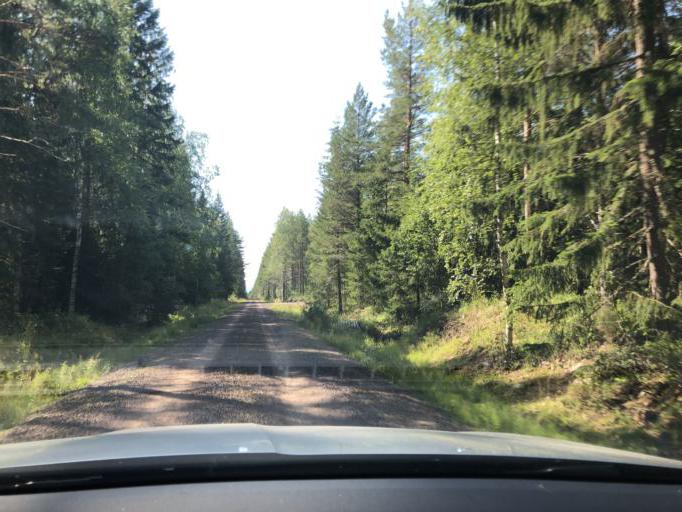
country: SE
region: Dalarna
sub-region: Orsa Kommun
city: Orsa
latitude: 61.2236
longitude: 14.7377
